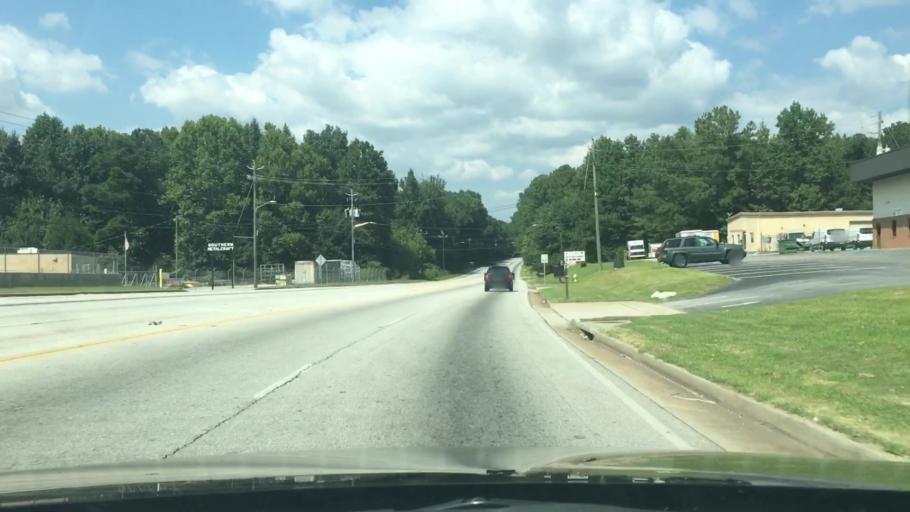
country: US
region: Georgia
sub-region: DeKalb County
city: Lithonia
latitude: 33.7073
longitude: -84.1302
